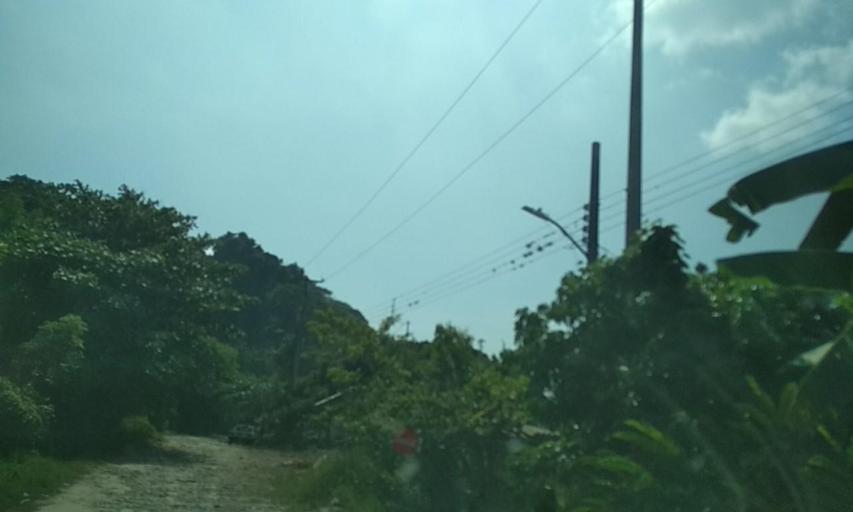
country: MX
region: Veracruz
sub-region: Atzalan
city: Colonias Pedernales
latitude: 20.0546
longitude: -97.0210
